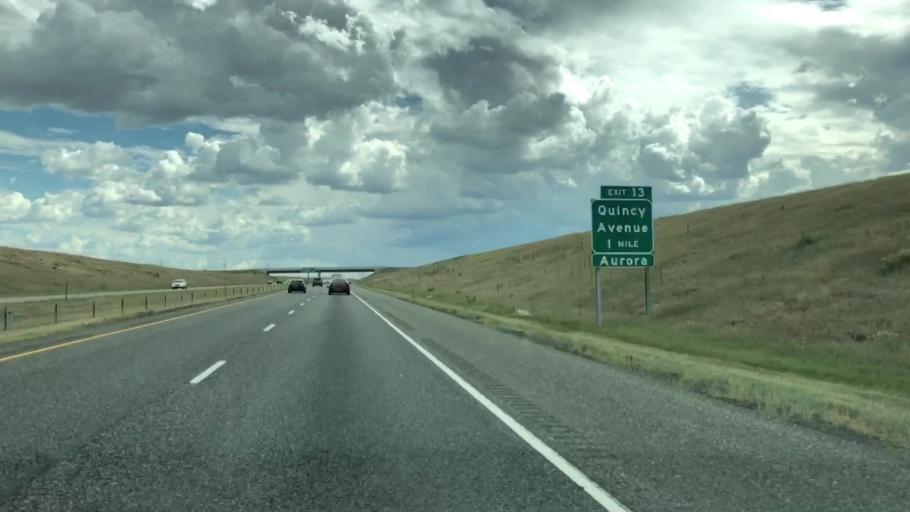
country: US
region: Colorado
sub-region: Adams County
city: Aurora
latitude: 39.6575
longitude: -104.7212
